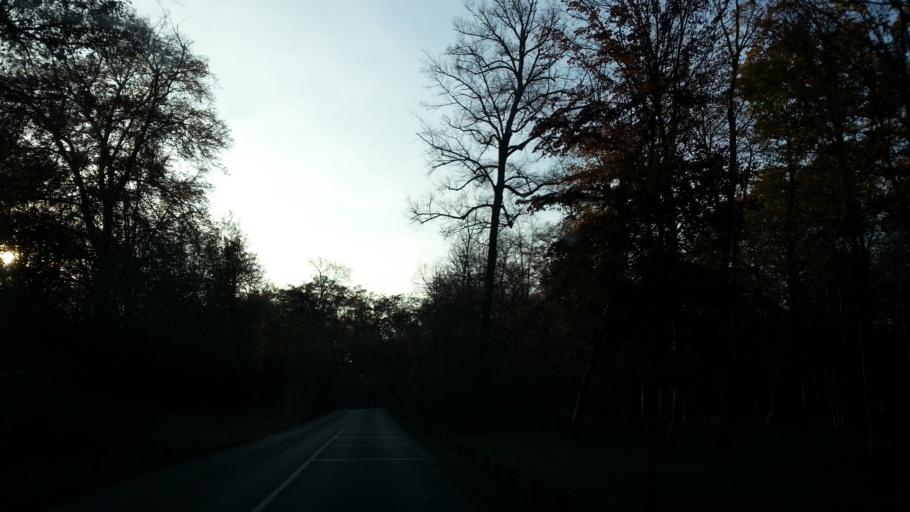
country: FR
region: Picardie
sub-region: Departement de l'Oise
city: Chantilly
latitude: 49.1867
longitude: 2.4730
